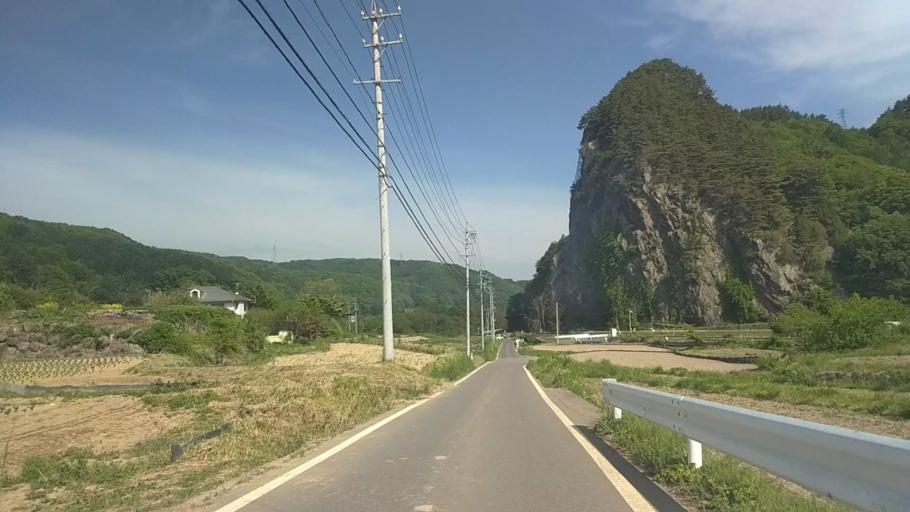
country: JP
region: Nagano
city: Saku
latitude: 36.1080
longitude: 138.4827
